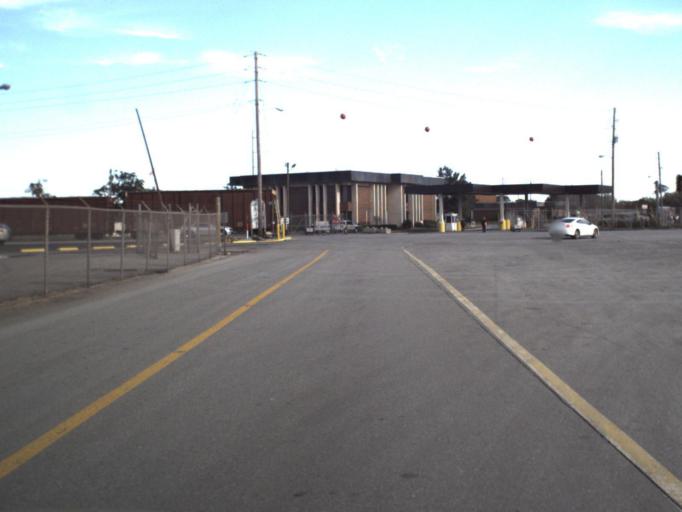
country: US
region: Florida
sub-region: Bay County
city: Upper Grand Lagoon
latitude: 30.1819
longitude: -85.7304
